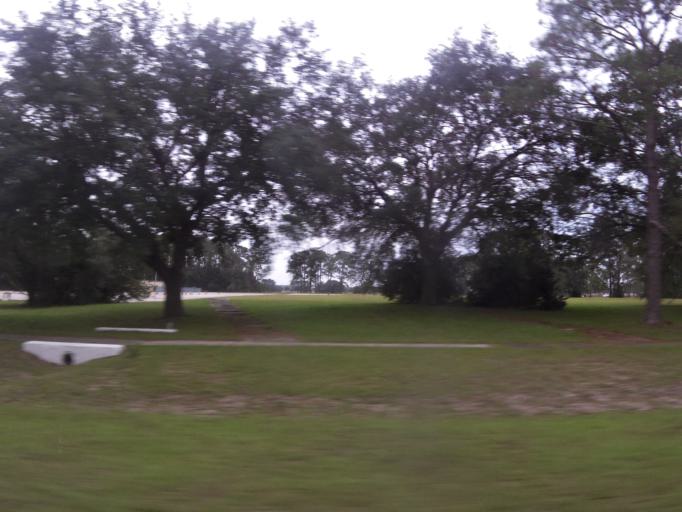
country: US
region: Florida
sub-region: Duval County
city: Baldwin
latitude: 30.2273
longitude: -81.8896
